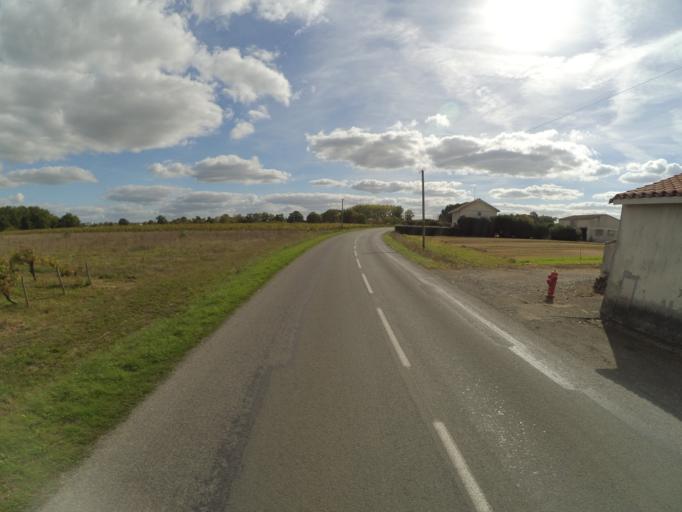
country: FR
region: Pays de la Loire
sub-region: Departement de la Loire-Atlantique
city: La Chapelle-Heulin
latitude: 47.2065
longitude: -1.3483
